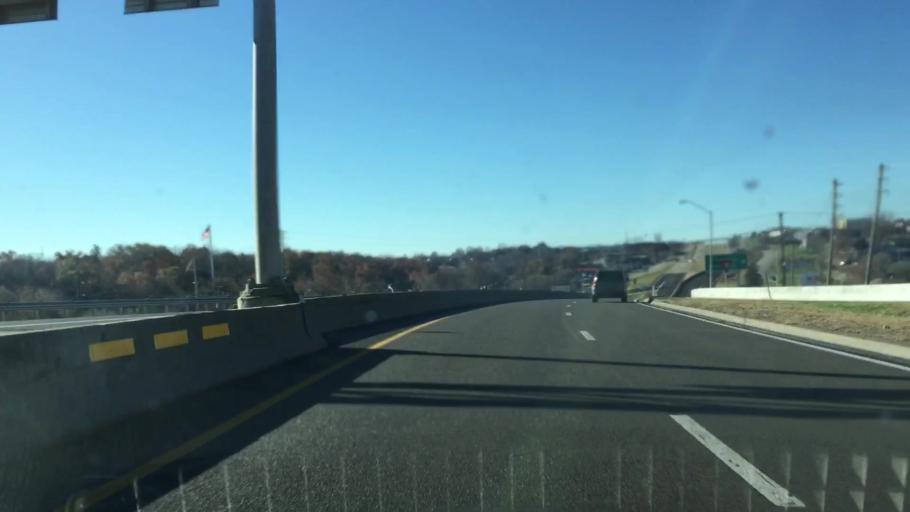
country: US
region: Missouri
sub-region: Cole County
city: Jefferson City
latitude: 38.5652
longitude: -92.1842
